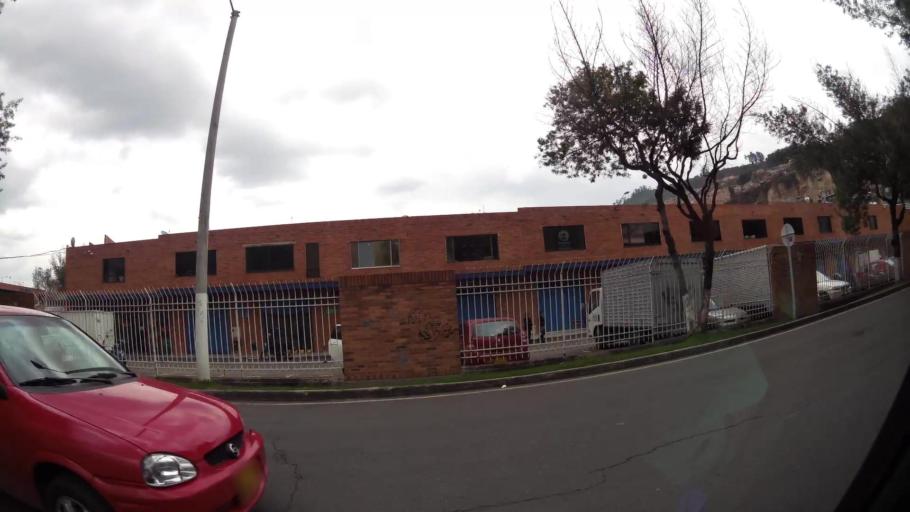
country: CO
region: Cundinamarca
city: La Calera
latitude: 4.7562
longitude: -74.0268
